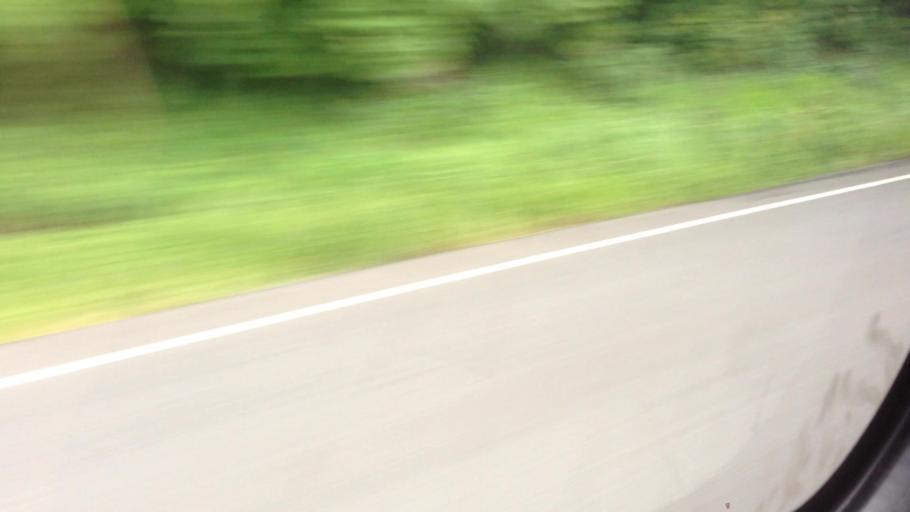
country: US
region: New York
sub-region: Dutchess County
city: Tivoli
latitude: 42.0407
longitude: -73.8944
